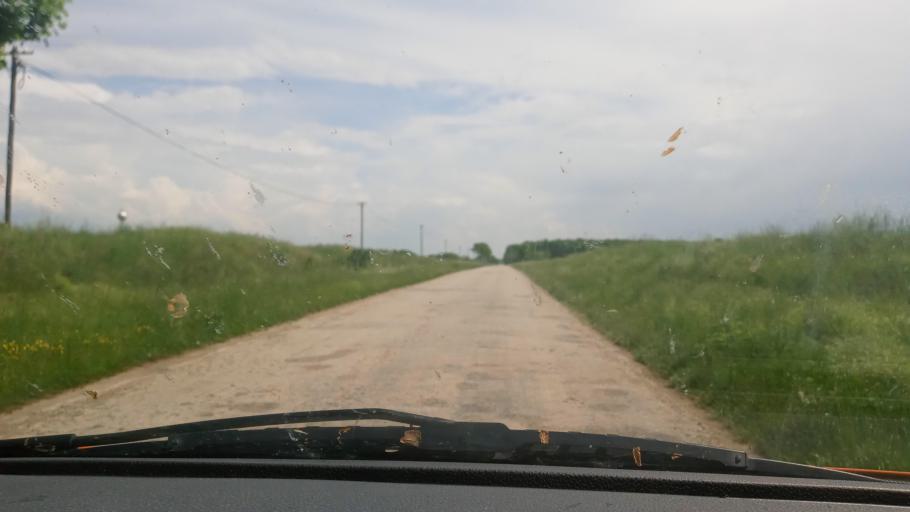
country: HU
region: Baranya
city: Siklos
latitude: 45.8091
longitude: 18.3413
